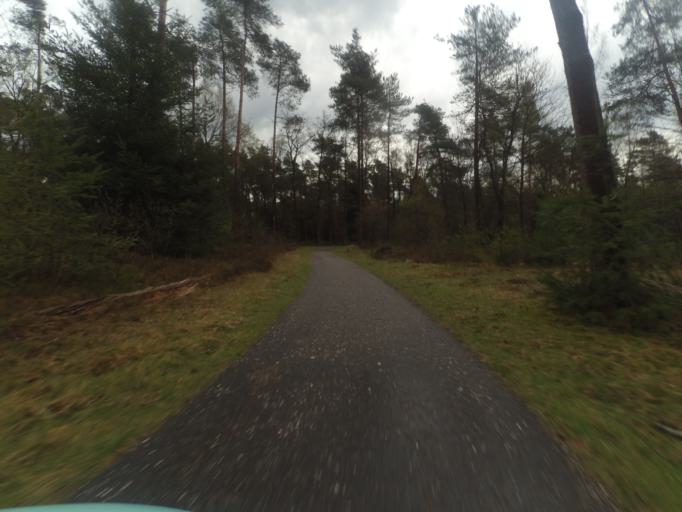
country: NL
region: Gelderland
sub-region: Gemeente Apeldoorn
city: Beekbergen
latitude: 52.1273
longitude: 5.9429
